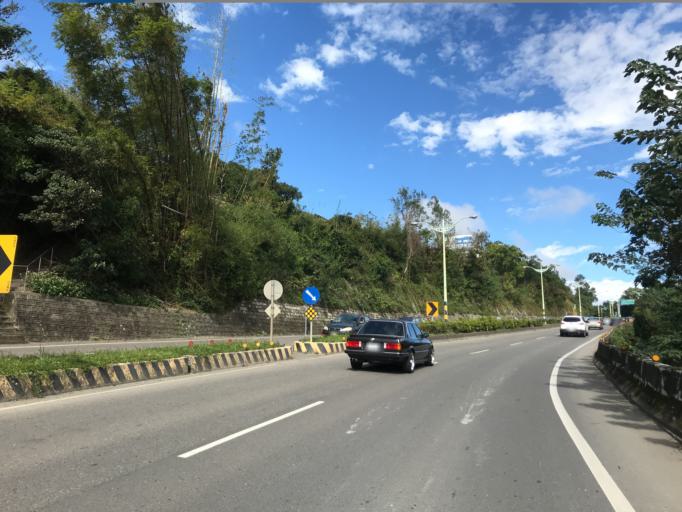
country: TW
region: Taiwan
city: Daxi
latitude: 24.8451
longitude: 121.2442
